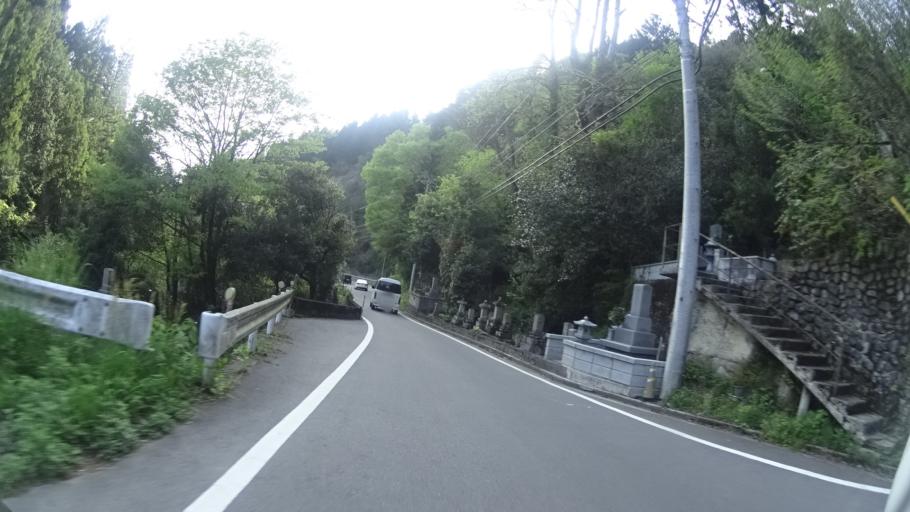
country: JP
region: Tokushima
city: Ikedacho
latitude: 33.8823
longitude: 133.9288
